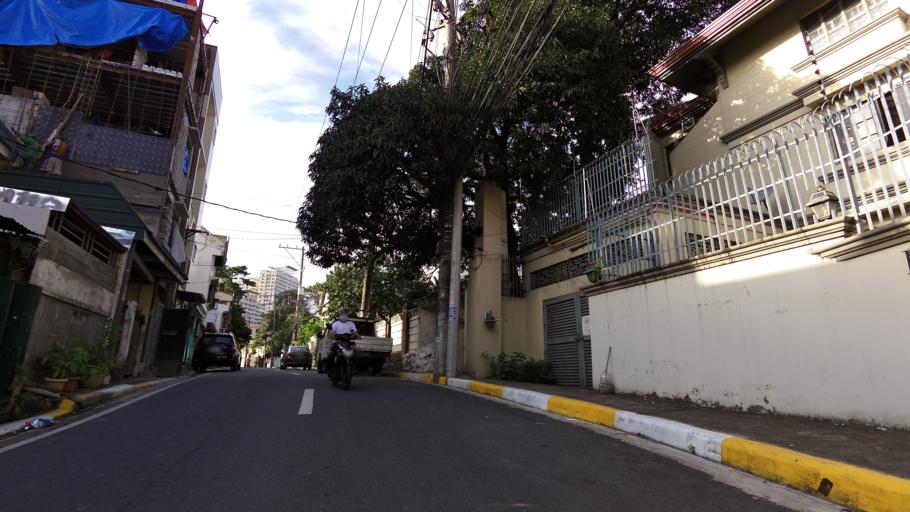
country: PH
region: Metro Manila
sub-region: San Juan
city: San Juan
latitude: 14.6092
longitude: 121.0331
